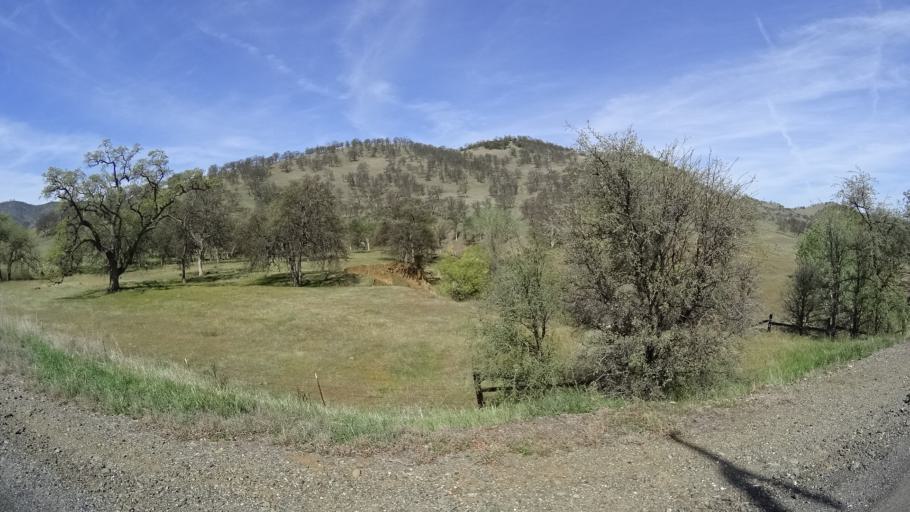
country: US
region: California
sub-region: Glenn County
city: Willows
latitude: 39.5315
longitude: -122.4563
